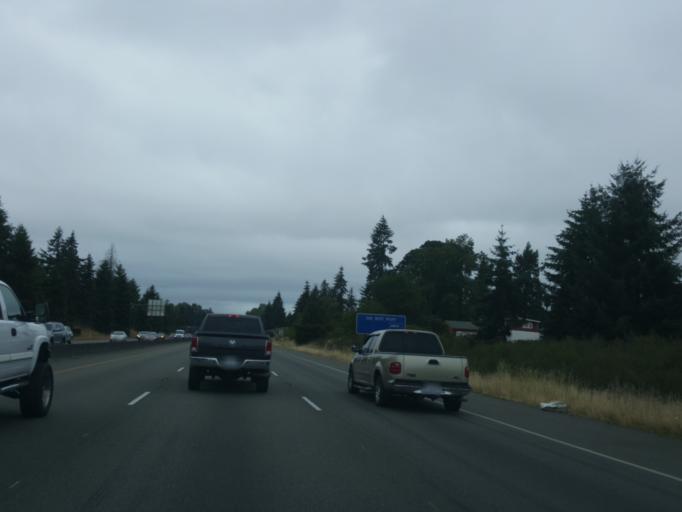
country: US
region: Washington
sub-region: Pierce County
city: Parkland
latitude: 47.1585
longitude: -122.4488
